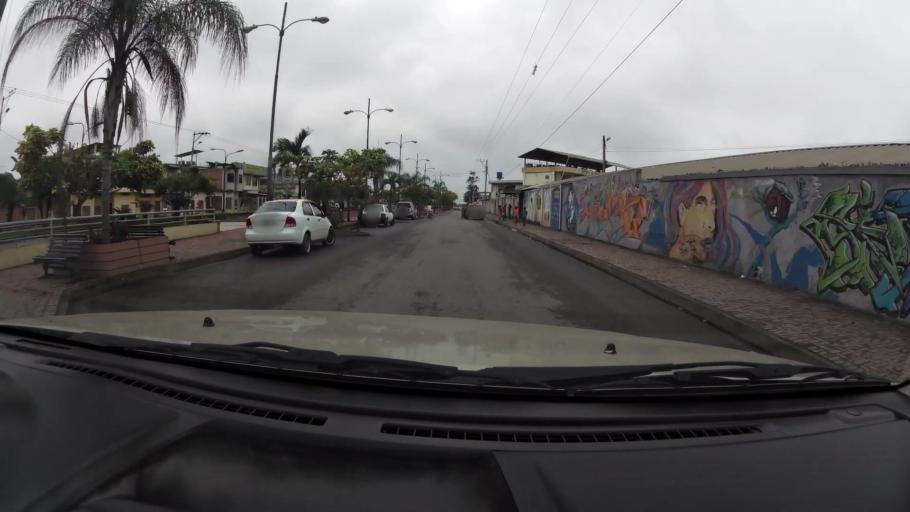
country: EC
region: El Oro
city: Pasaje
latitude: -3.3317
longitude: -79.8106
